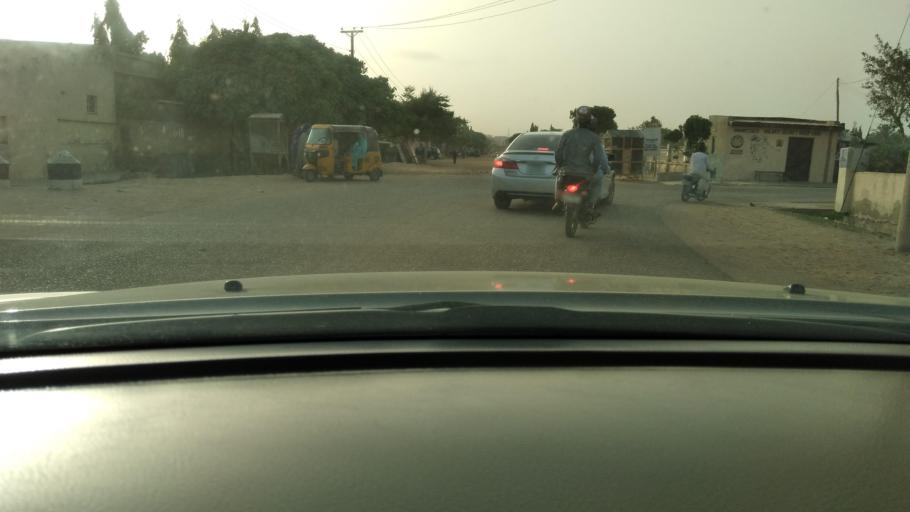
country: NG
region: Kano
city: Kano
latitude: 11.9548
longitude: 8.5228
